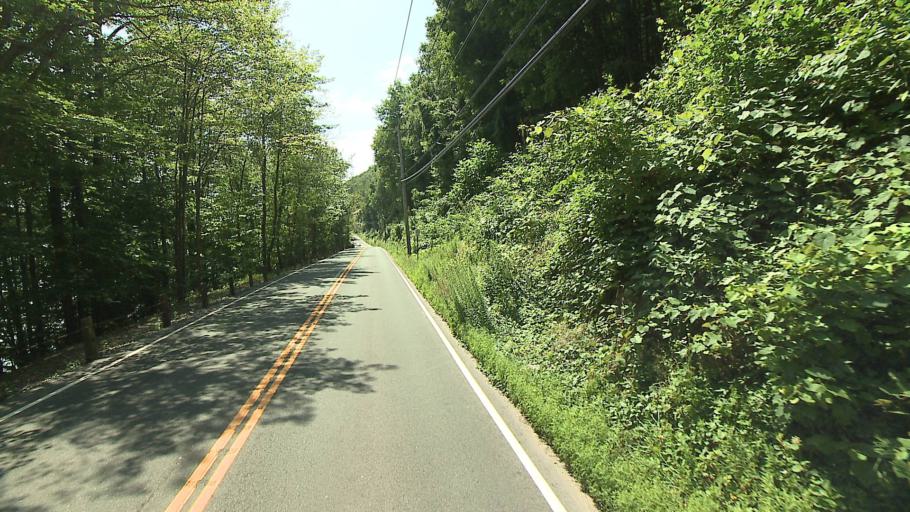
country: US
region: New York
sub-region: Putnam County
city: Putnam Lake
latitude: 41.4966
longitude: -73.4694
